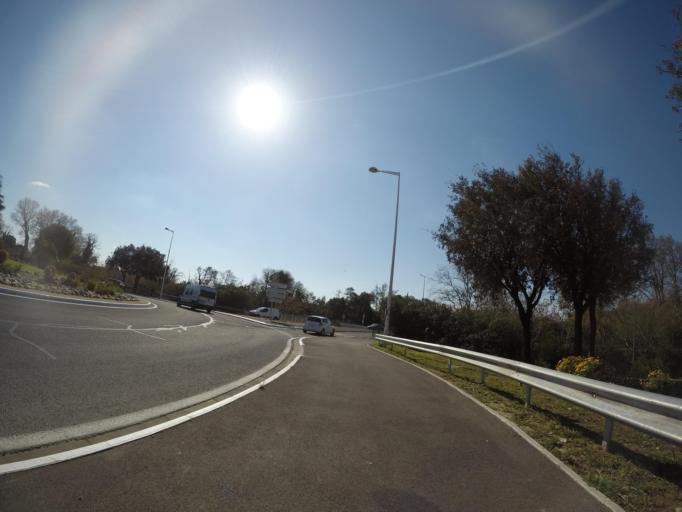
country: FR
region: Languedoc-Roussillon
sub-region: Departement des Pyrenees-Orientales
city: Perpignan
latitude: 42.7074
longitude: 2.9090
